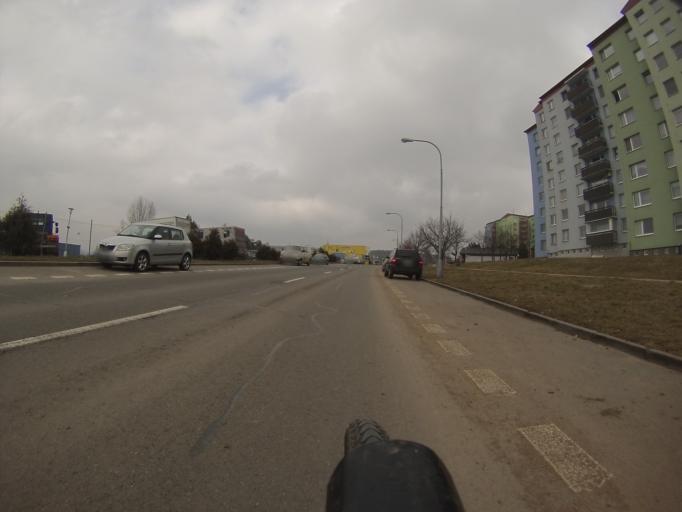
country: CZ
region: South Moravian
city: Bilovice nad Svitavou
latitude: 49.2080
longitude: 16.6734
